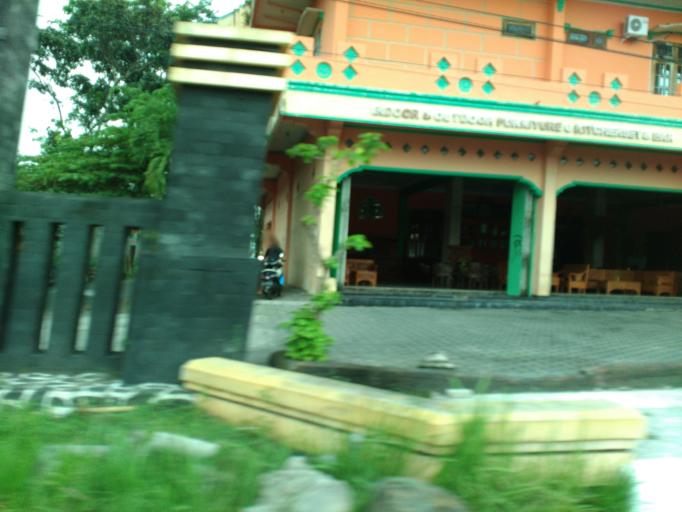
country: ID
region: Central Java
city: Gatak
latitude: -7.6088
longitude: 110.7017
